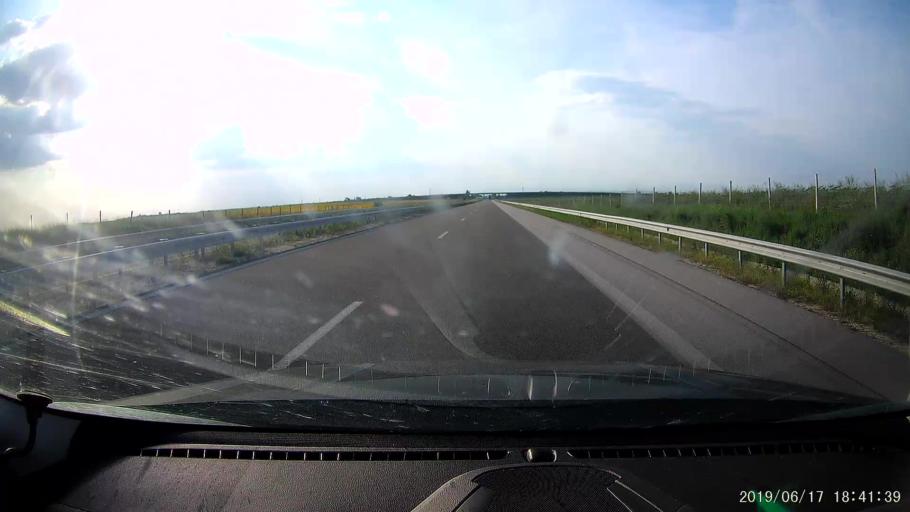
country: BG
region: Stara Zagora
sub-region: Obshtina Chirpan
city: Chirpan
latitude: 42.1763
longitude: 25.2519
